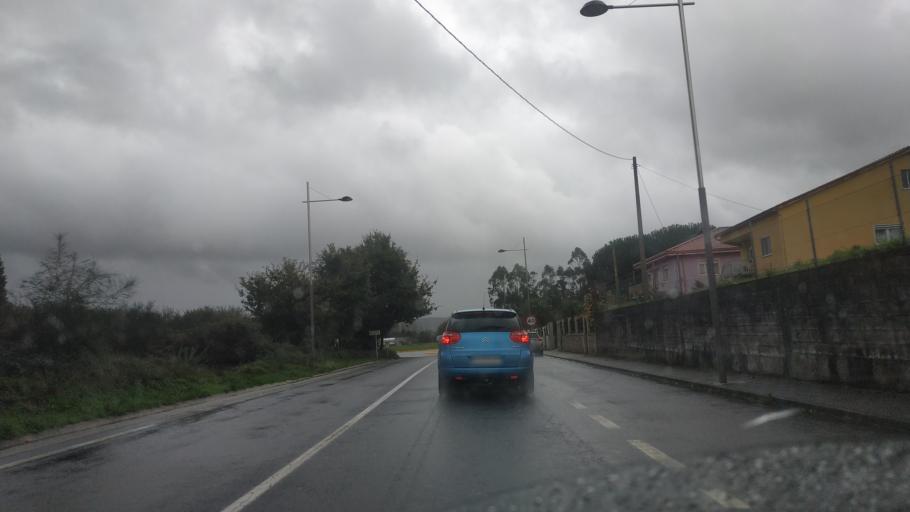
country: ES
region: Galicia
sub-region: Provincia da Coruna
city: Negreira
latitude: 42.9215
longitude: -8.7344
